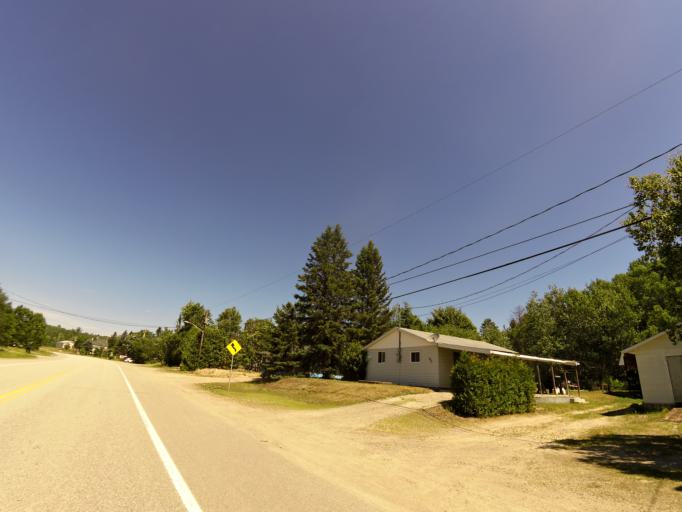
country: CA
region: Quebec
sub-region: Abitibi-Temiscamingue
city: Temiscaming
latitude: 46.7458
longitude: -79.0707
